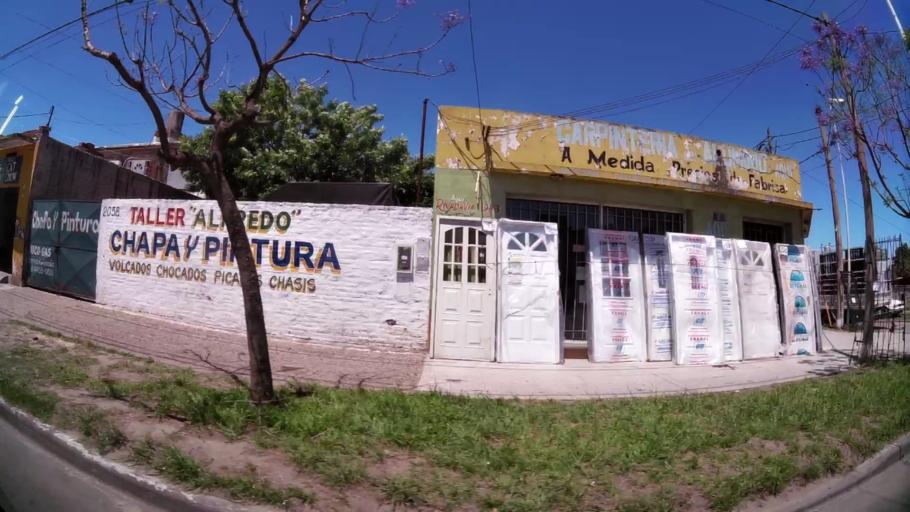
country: AR
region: Buenos Aires
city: Hurlingham
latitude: -34.5065
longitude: -58.6997
